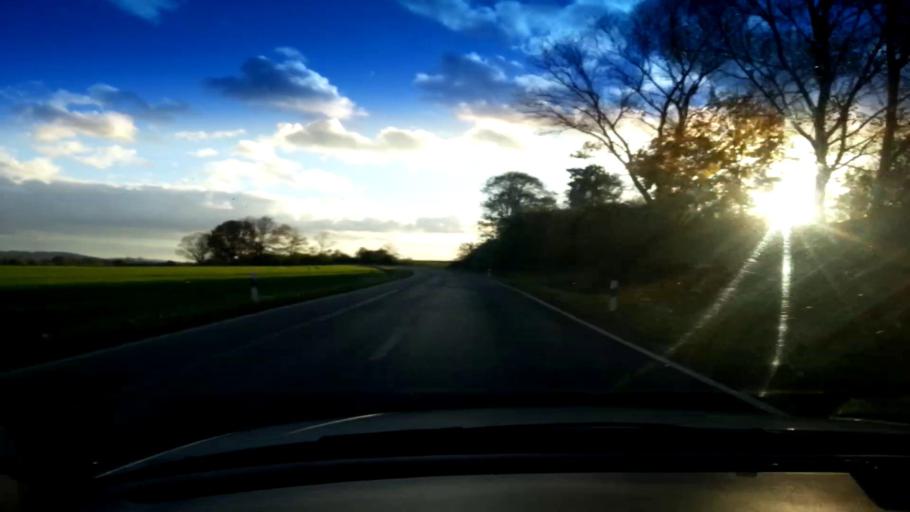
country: DE
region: Bavaria
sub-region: Upper Franconia
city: Zapfendorf
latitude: 50.0408
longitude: 10.9201
